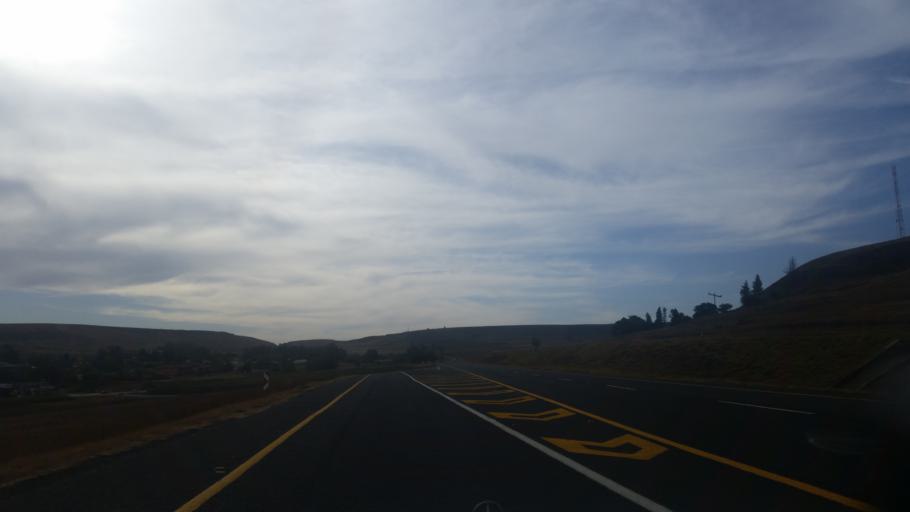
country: ZA
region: Orange Free State
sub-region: Thabo Mofutsanyana District Municipality
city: Phuthaditjhaba
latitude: -28.3093
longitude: 28.7130
